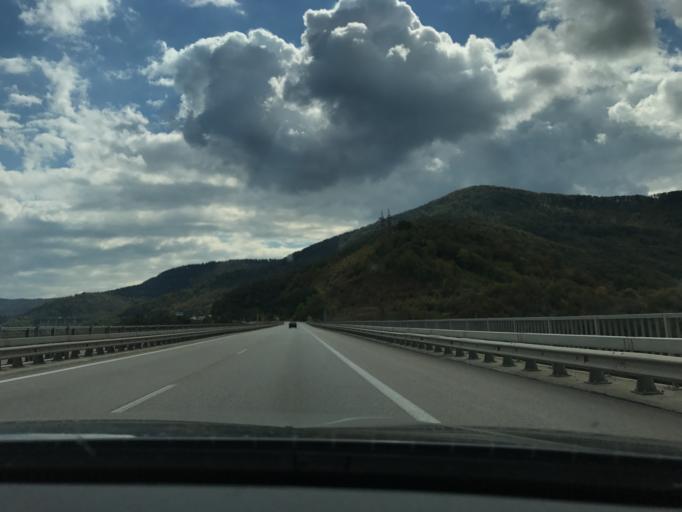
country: BG
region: Sofiya
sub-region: Obshtina Botevgrad
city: Botevgrad
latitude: 42.8260
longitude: 23.7966
